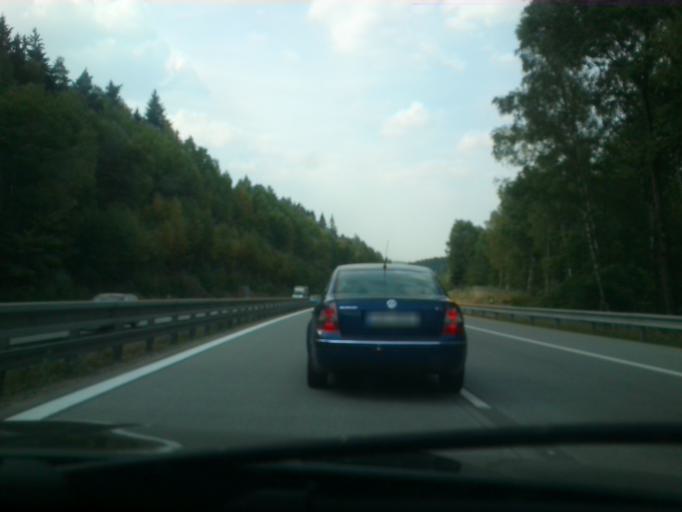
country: CZ
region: Central Bohemia
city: Vlasim
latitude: 49.7622
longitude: 14.9529
